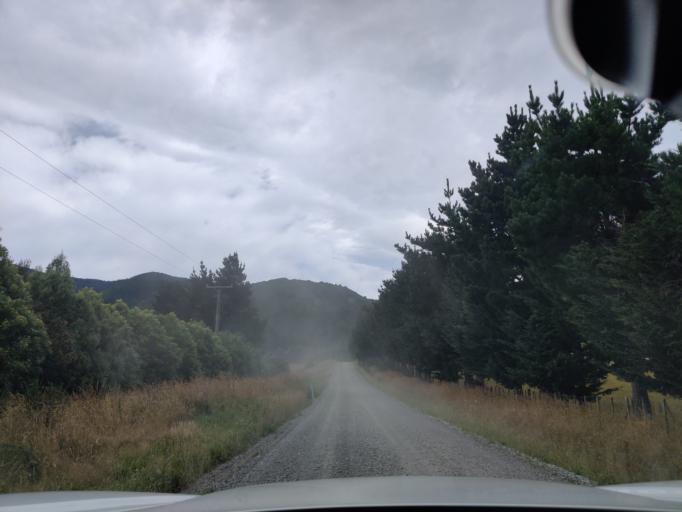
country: NZ
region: Wellington
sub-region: Masterton District
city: Masterton
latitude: -41.0383
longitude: 175.4022
